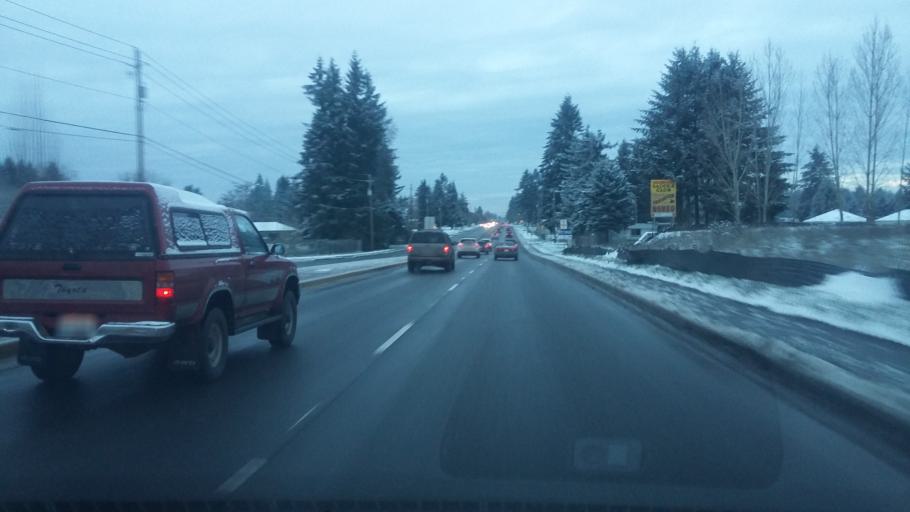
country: US
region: Washington
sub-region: Clark County
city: Five Corners
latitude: 45.6964
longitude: -122.5527
